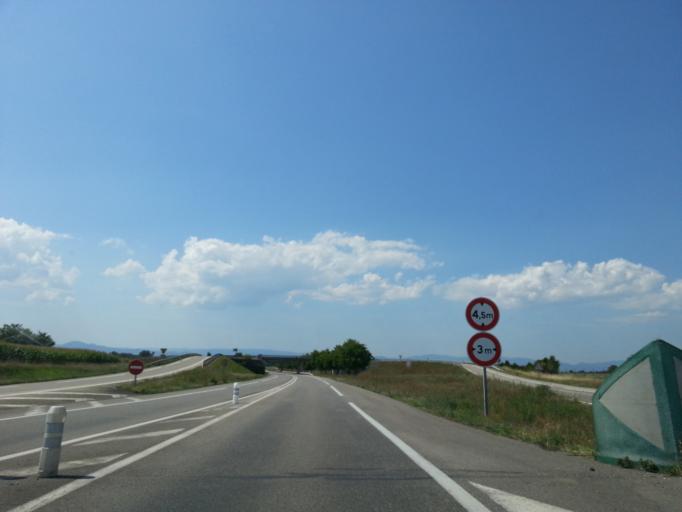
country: FR
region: Alsace
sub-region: Departement du Haut-Rhin
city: Wolfgantzen
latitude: 48.0320
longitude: 7.5060
